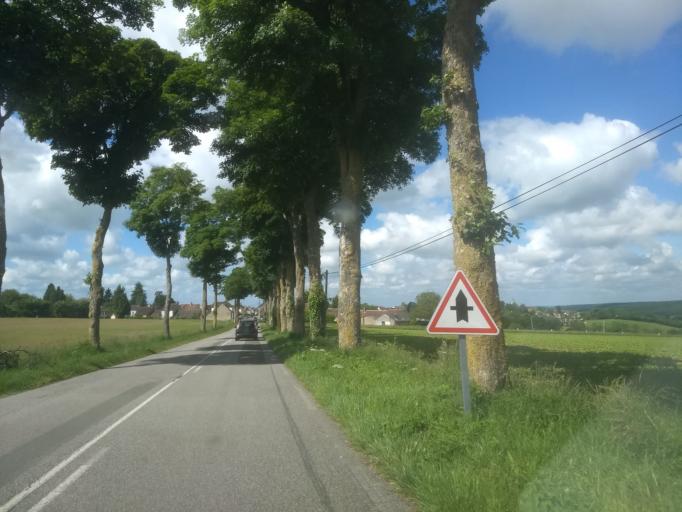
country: FR
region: Lower Normandy
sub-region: Departement de l'Orne
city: Belleme
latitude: 48.3772
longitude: 0.5775
